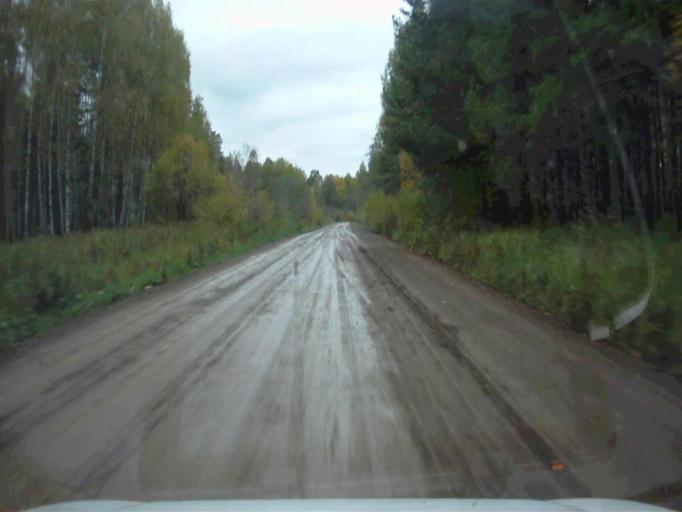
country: RU
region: Chelyabinsk
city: Nyazepetrovsk
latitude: 56.0994
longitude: 59.3921
